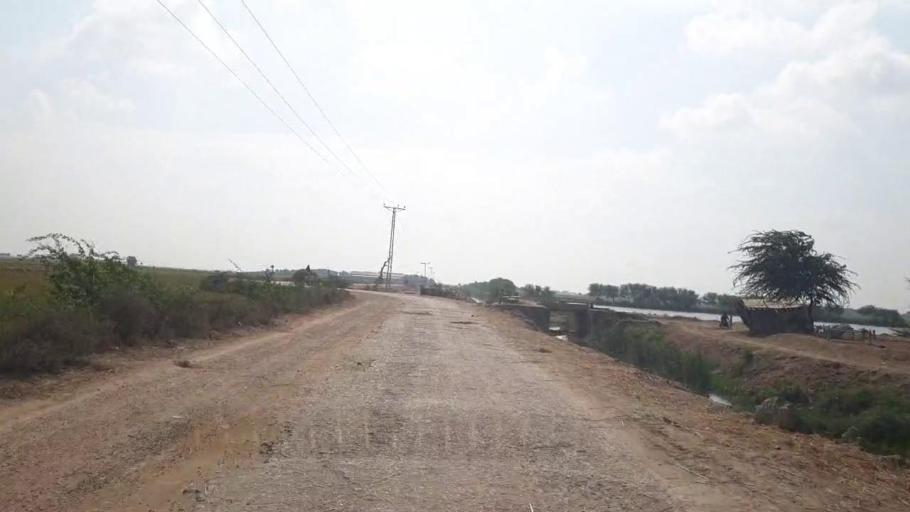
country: PK
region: Sindh
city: Kario
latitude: 24.6427
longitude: 68.5442
